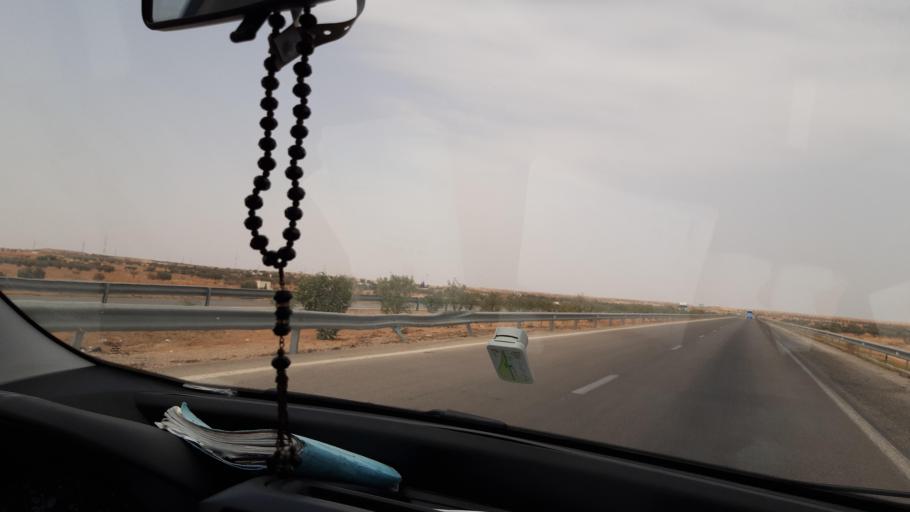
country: TN
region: Safaqis
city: Sfax
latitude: 34.7395
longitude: 10.5958
